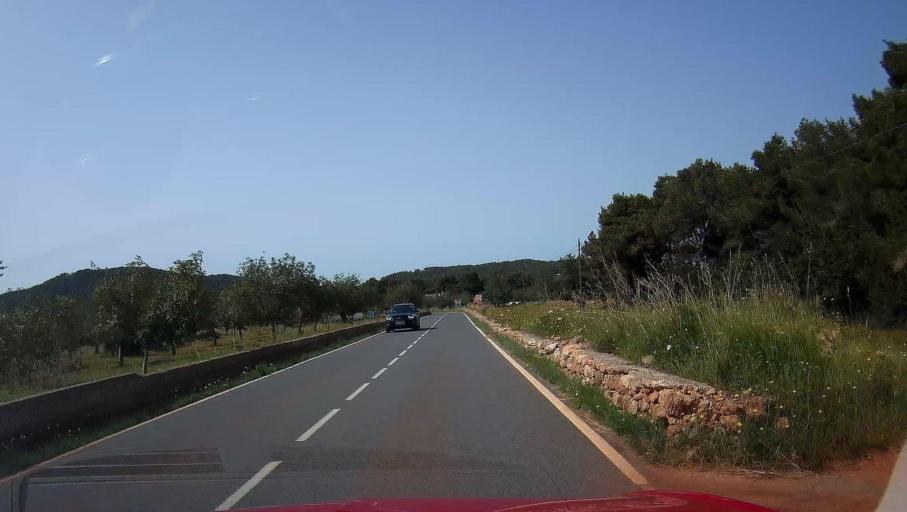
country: ES
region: Balearic Islands
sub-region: Illes Balears
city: Sant Joan de Labritja
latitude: 39.0508
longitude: 1.5728
